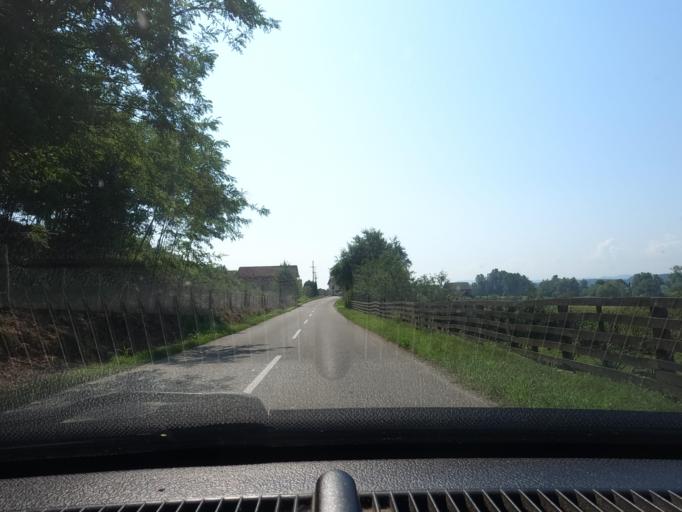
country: RS
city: Kozjak
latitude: 44.5539
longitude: 19.3234
